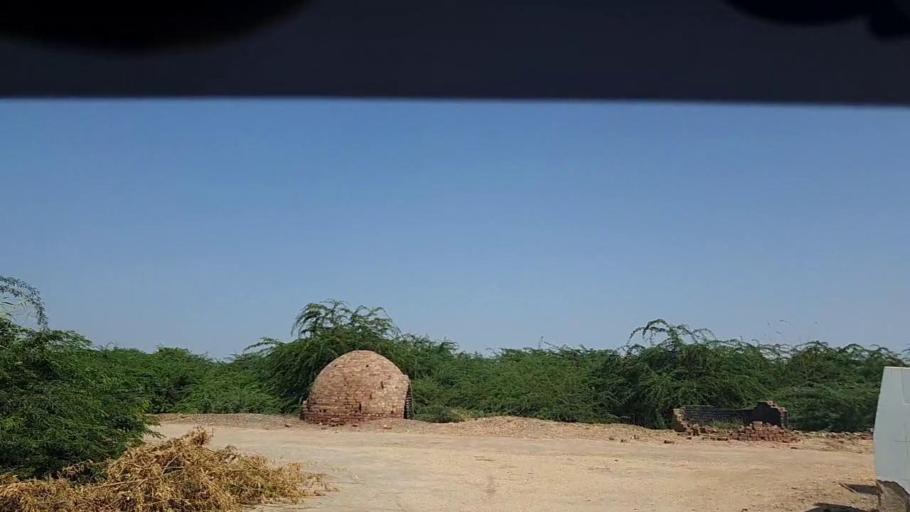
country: PK
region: Sindh
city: Badin
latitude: 24.4621
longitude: 68.7793
